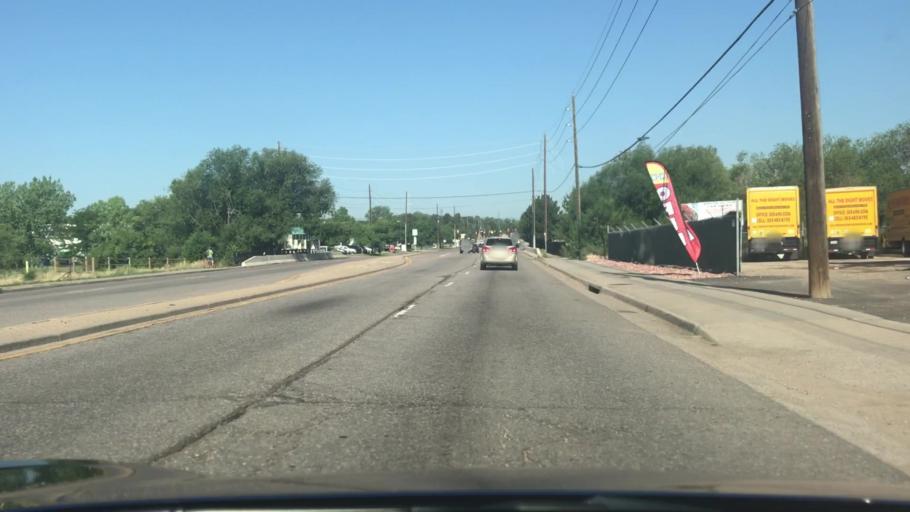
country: US
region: Colorado
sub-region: Arapahoe County
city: Glendale
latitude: 39.6749
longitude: -104.8928
